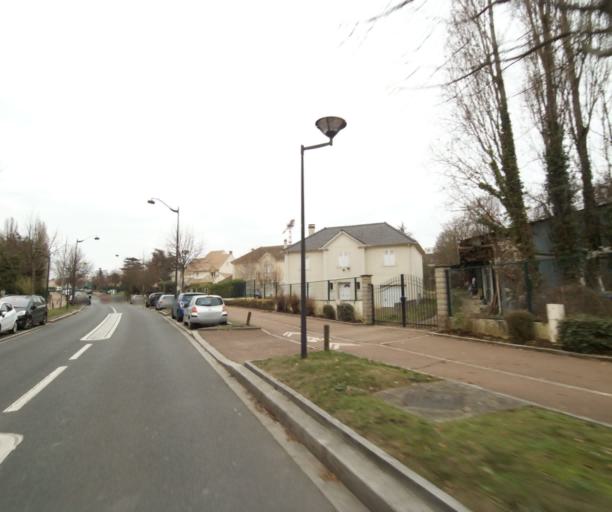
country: FR
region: Ile-de-France
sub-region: Departement des Hauts-de-Seine
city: Saint-Cloud
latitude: 48.8572
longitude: 2.1960
